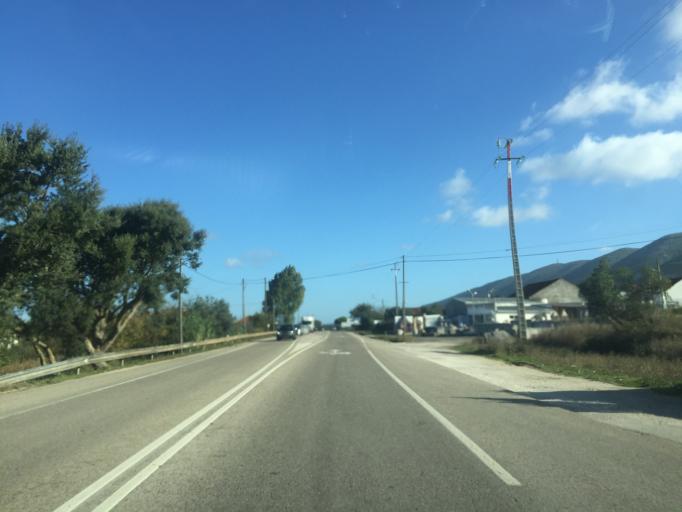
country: PT
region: Leiria
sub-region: Alcobaca
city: Aljubarrota
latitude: 39.5258
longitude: -8.9102
